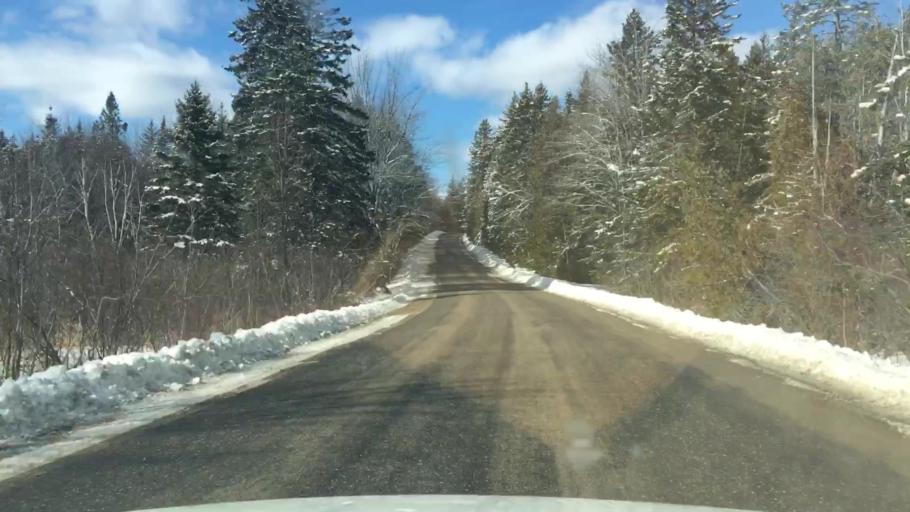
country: US
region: Maine
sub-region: Washington County
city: Machias
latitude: 44.6840
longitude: -67.4579
